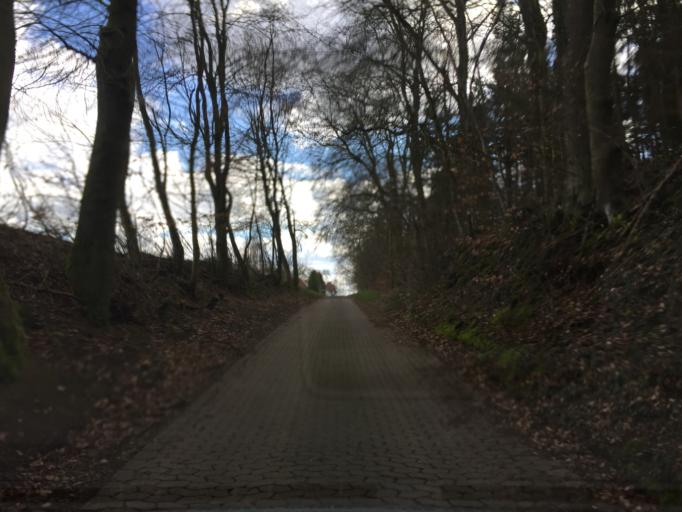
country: DE
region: Lower Saxony
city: Bruchhausen-Vilsen
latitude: 52.8018
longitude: 8.9967
